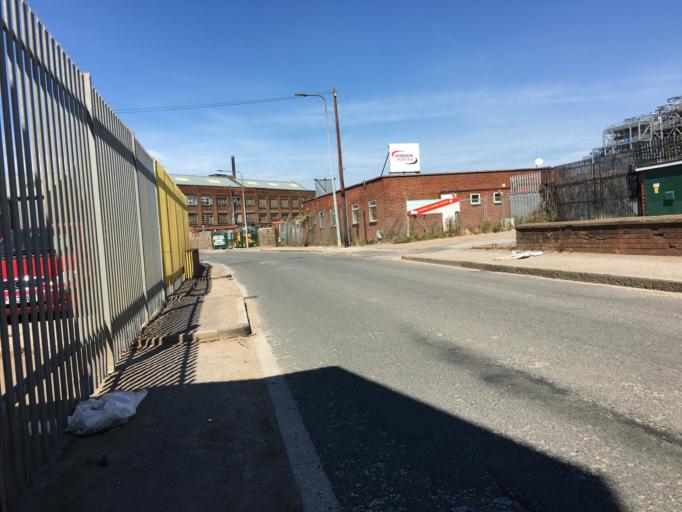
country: GB
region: England
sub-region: City of Kingston upon Hull
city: Hull
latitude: 53.7551
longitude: -0.3308
